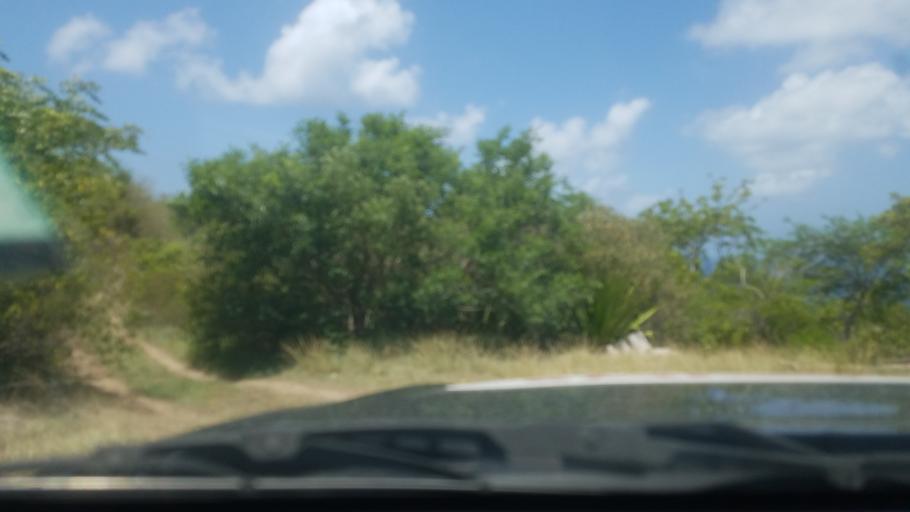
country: LC
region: Vieux-Fort
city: Vieux Fort
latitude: 13.7143
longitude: -60.9523
